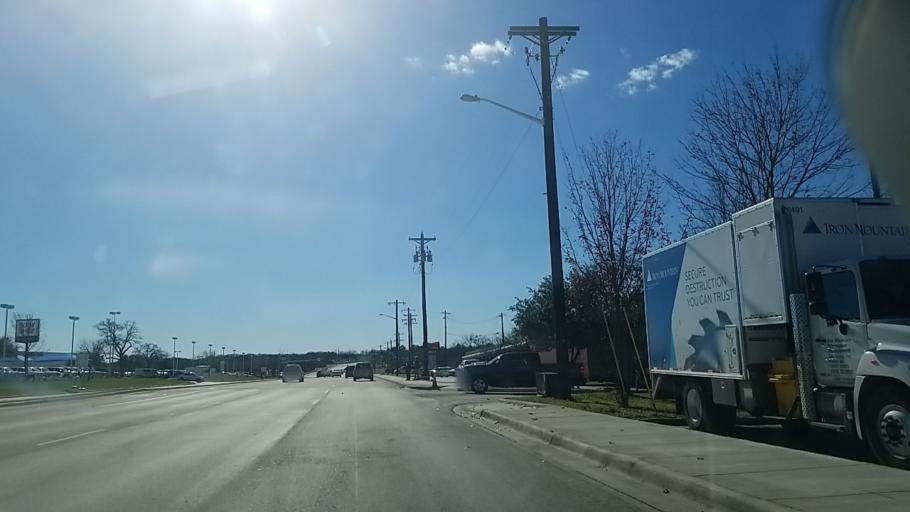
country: US
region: Texas
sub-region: Denton County
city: Corinth
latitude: 33.1722
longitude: -97.0907
